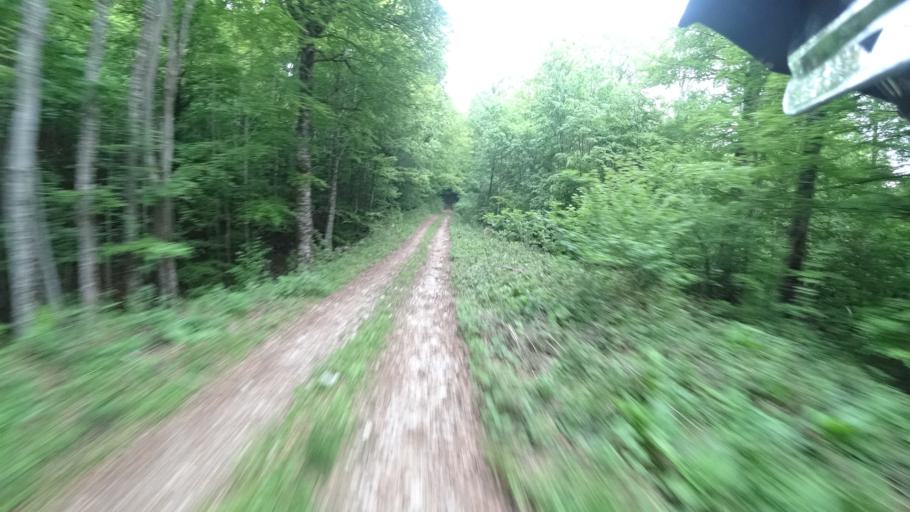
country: HR
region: Karlovacka
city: Plaski
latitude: 45.0117
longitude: 15.3483
